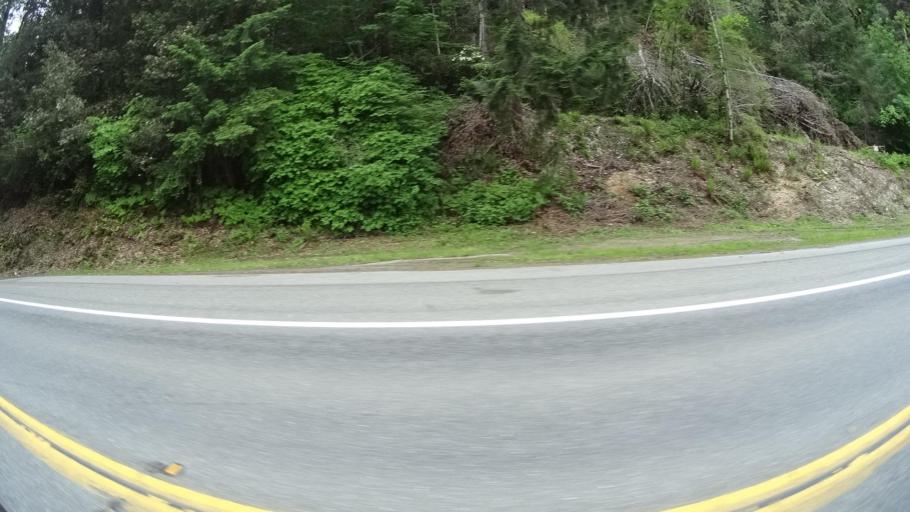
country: US
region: California
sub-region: Humboldt County
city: Willow Creek
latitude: 40.9987
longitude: -123.6440
